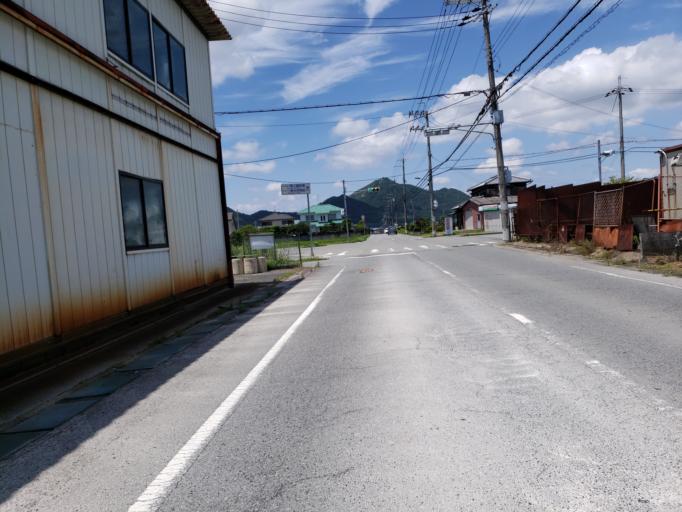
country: JP
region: Hyogo
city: Kakogawacho-honmachi
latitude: 34.8046
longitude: 134.8236
